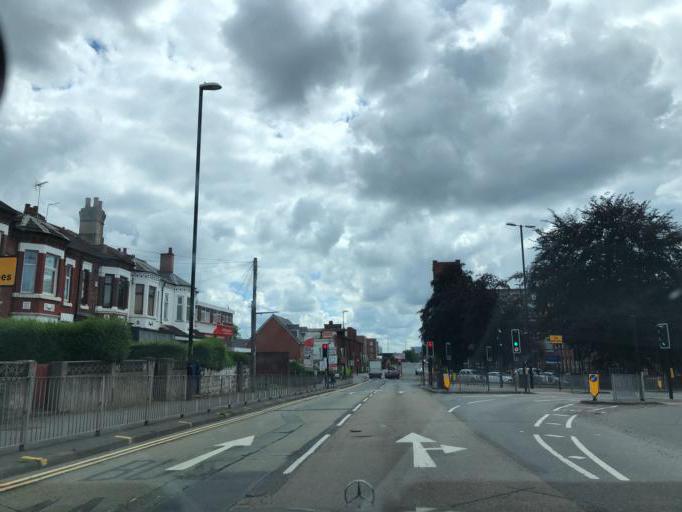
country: GB
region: England
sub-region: Coventry
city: Coventry
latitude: 52.4256
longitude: -1.5017
